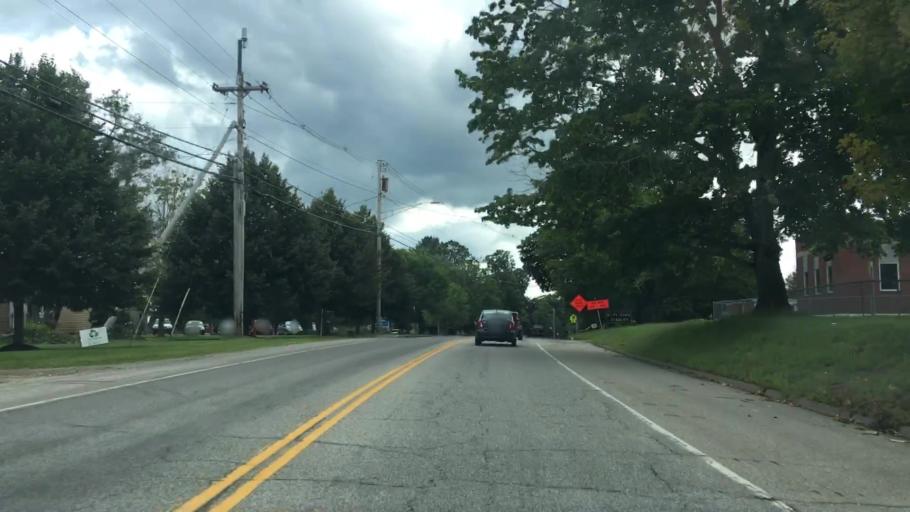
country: US
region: Maine
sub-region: York County
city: North Berwick
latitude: 43.3116
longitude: -70.7384
